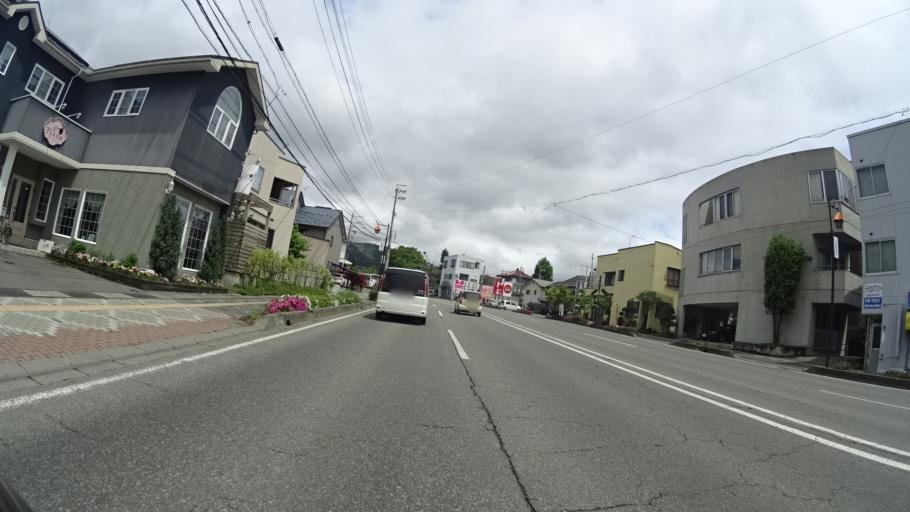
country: JP
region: Nagano
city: Nagano-shi
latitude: 36.6680
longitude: 138.1976
